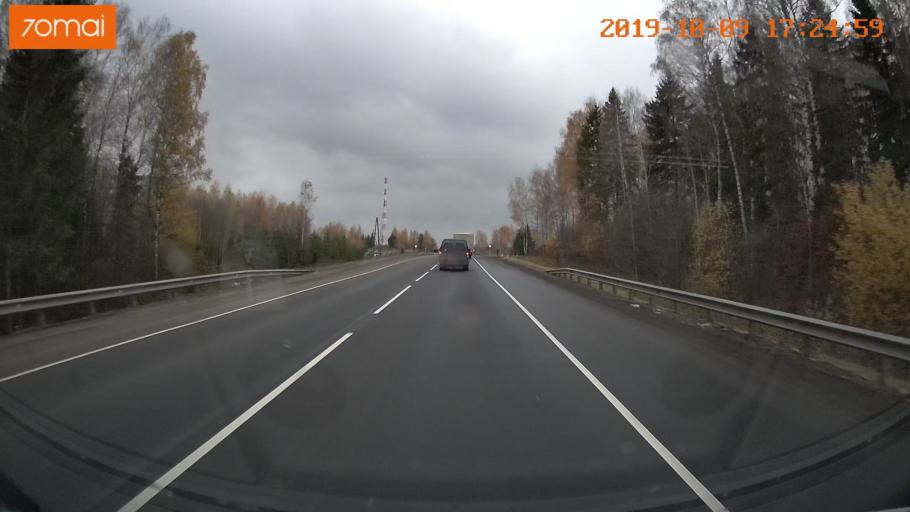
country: RU
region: Ivanovo
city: Furmanov
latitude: 57.1823
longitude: 41.0974
